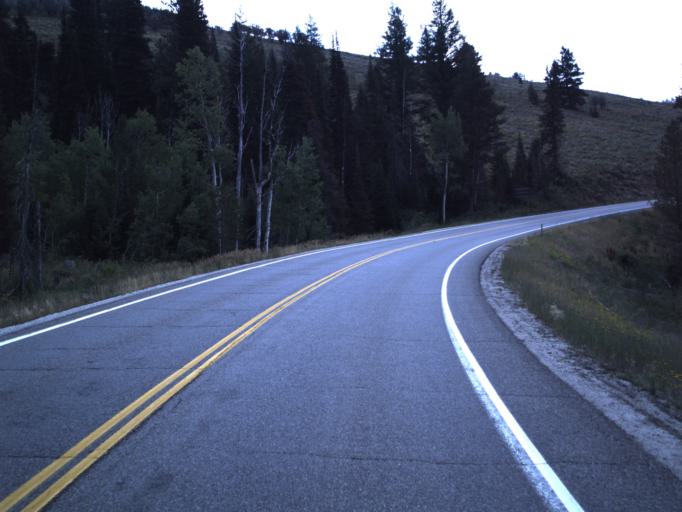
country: US
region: Idaho
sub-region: Bear Lake County
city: Paris
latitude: 41.9646
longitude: -111.5212
